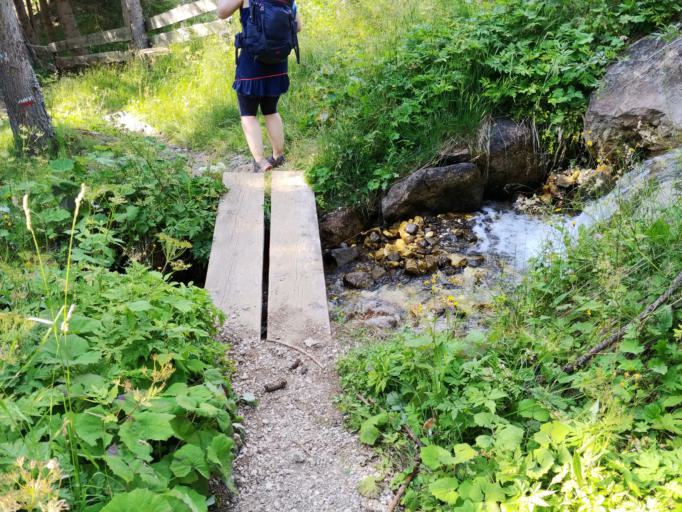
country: IT
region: Trentino-Alto Adige
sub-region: Bolzano
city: Santa Cristina Valgardena
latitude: 46.5500
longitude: 11.7290
